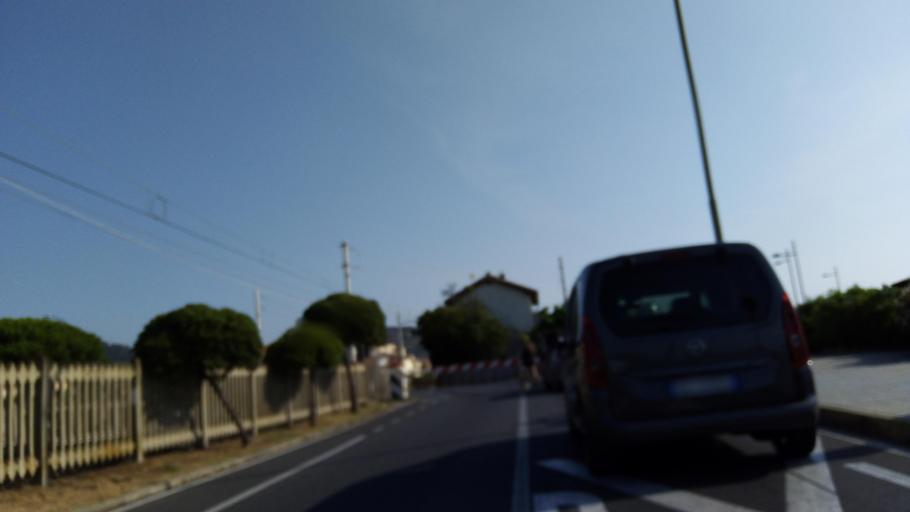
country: IT
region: Liguria
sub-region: Provincia di Savona
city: Loano
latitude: 44.1367
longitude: 8.2664
